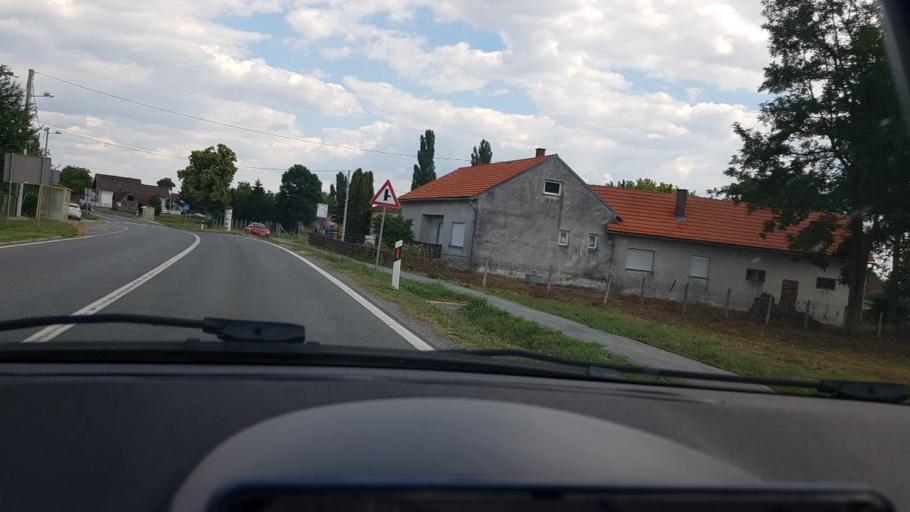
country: HR
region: Bjelovarsko-Bilogorska
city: Zdralovi
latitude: 45.8534
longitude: 16.9297
